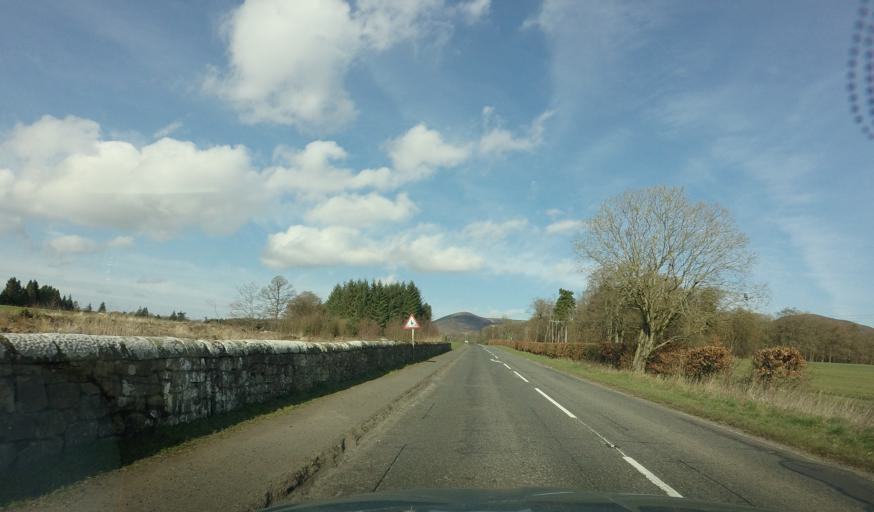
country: GB
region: Scotland
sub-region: Midlothian
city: Penicuik
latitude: 55.8261
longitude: -3.2445
